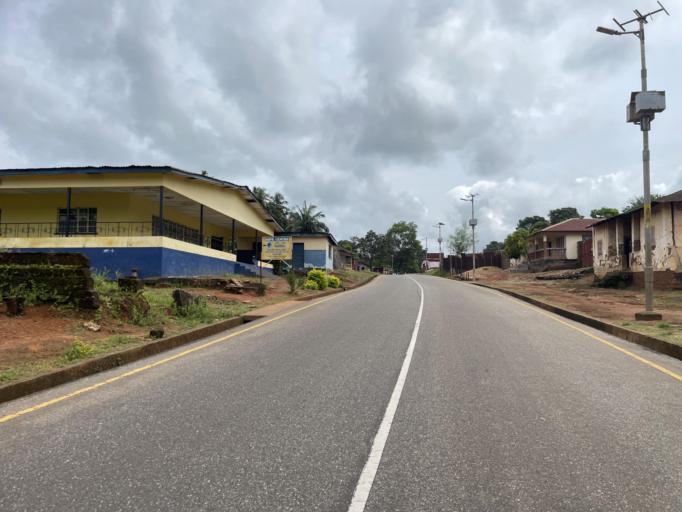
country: SL
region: Northern Province
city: Kambia
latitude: 9.1278
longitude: -12.9191
